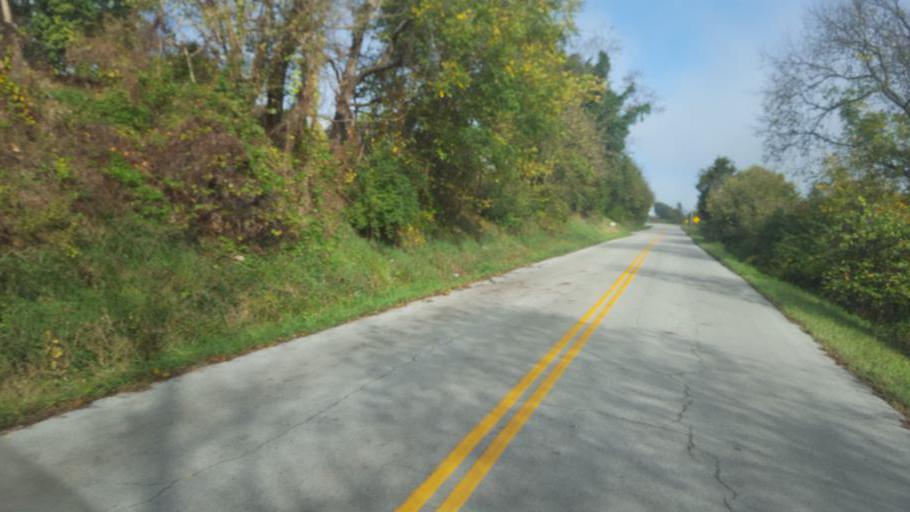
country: US
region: Kentucky
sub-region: Mason County
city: Maysville
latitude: 38.5547
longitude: -83.7721
